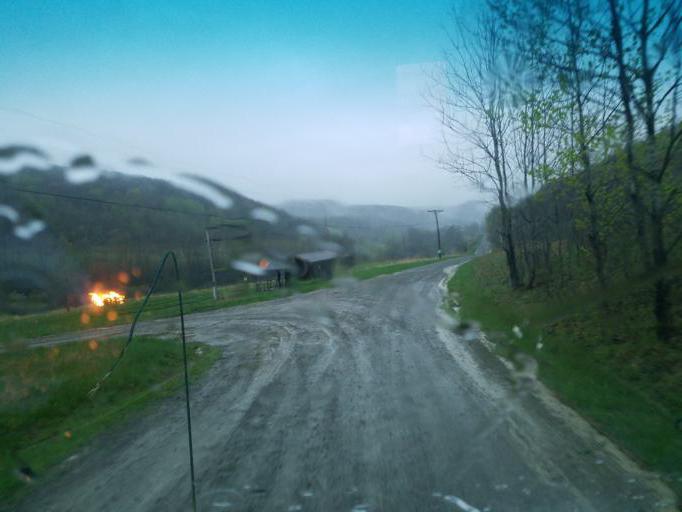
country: US
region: Pennsylvania
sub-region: Tioga County
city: Westfield
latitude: 41.9011
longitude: -77.7158
